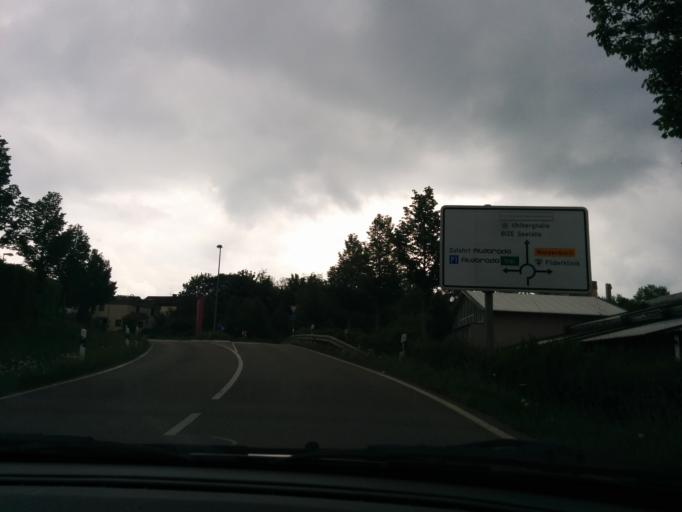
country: DE
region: Baden-Wuerttemberg
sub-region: Regierungsbezirk Stuttgart
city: Filderstadt
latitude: 48.6515
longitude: 9.2048
